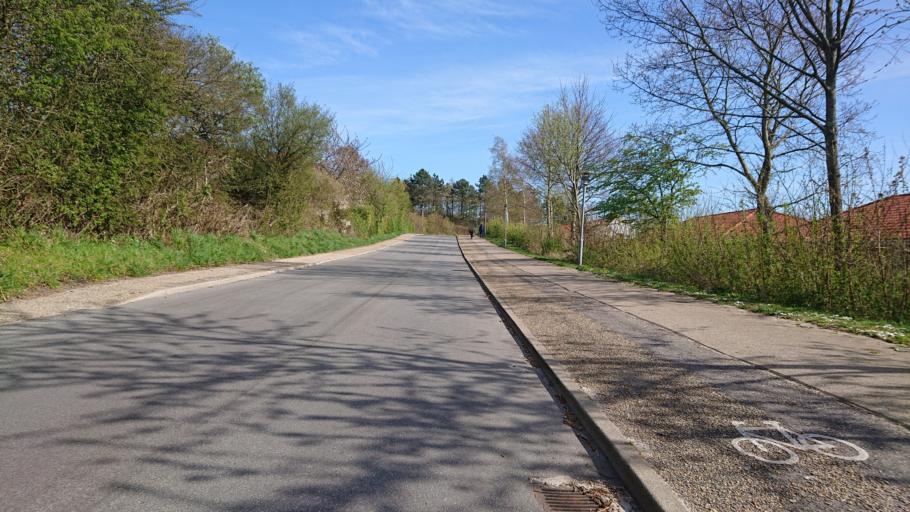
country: DK
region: South Denmark
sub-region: Nyborg Kommune
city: Nyborg
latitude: 55.3042
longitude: 10.7676
